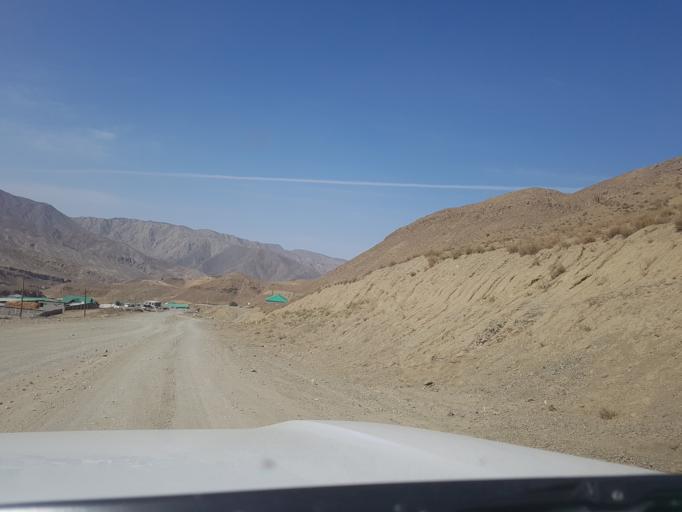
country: TM
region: Ahal
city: Baharly
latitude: 38.4506
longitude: 57.0468
